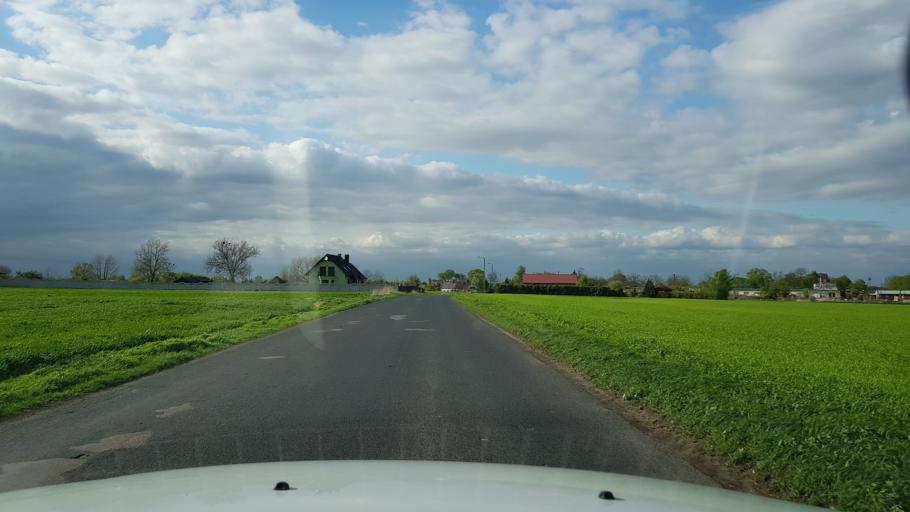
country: PL
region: West Pomeranian Voivodeship
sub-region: Powiat pyrzycki
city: Przelewice
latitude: 53.1174
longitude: 15.0593
